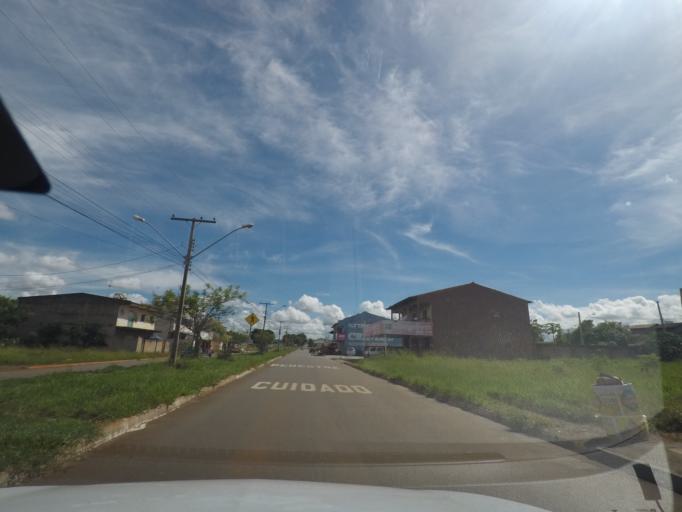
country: BR
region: Goias
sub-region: Goiania
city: Goiania
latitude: -16.7194
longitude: -49.3449
